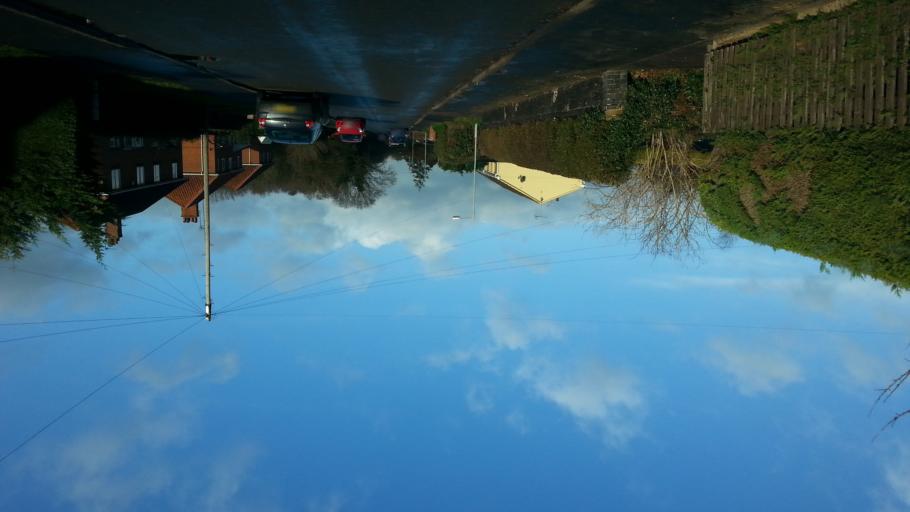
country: GB
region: England
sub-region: Norfolk
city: Ditchingham
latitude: 52.4688
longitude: 1.4467
